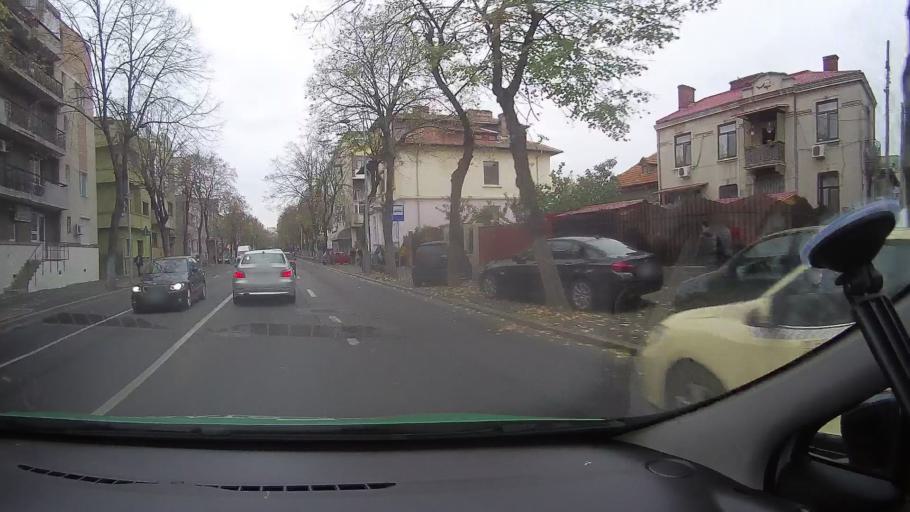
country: RO
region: Constanta
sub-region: Municipiul Constanta
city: Constanta
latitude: 44.1758
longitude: 28.6461
